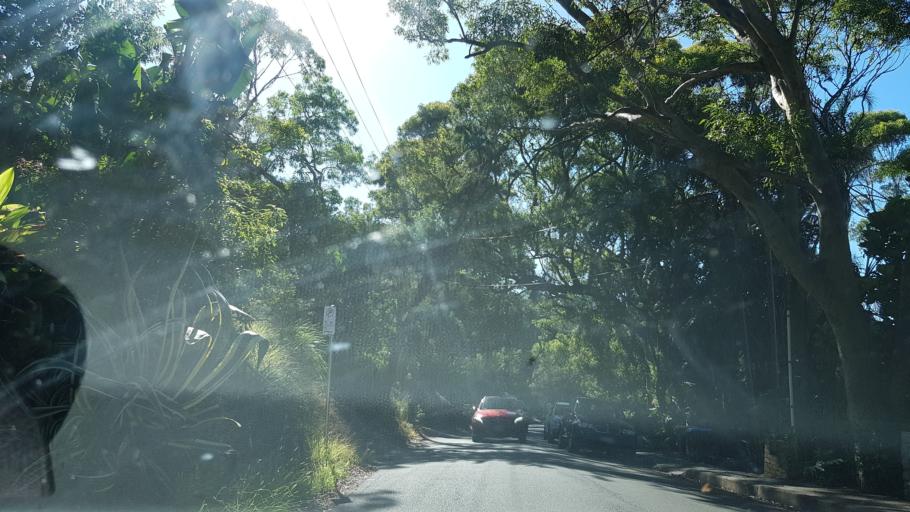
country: AU
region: New South Wales
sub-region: Pittwater
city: Palm Beach
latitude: -33.6175
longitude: 151.3339
